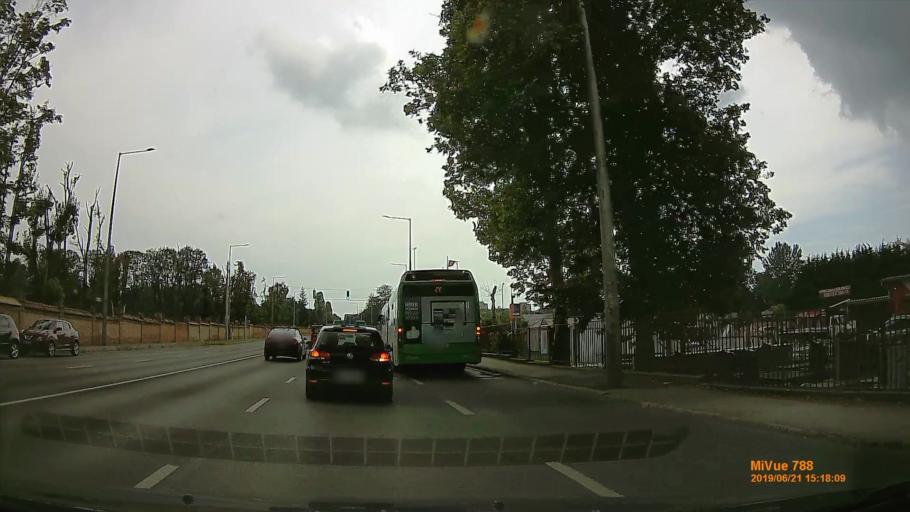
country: HU
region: Baranya
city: Pecs
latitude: 46.0524
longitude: 18.2312
